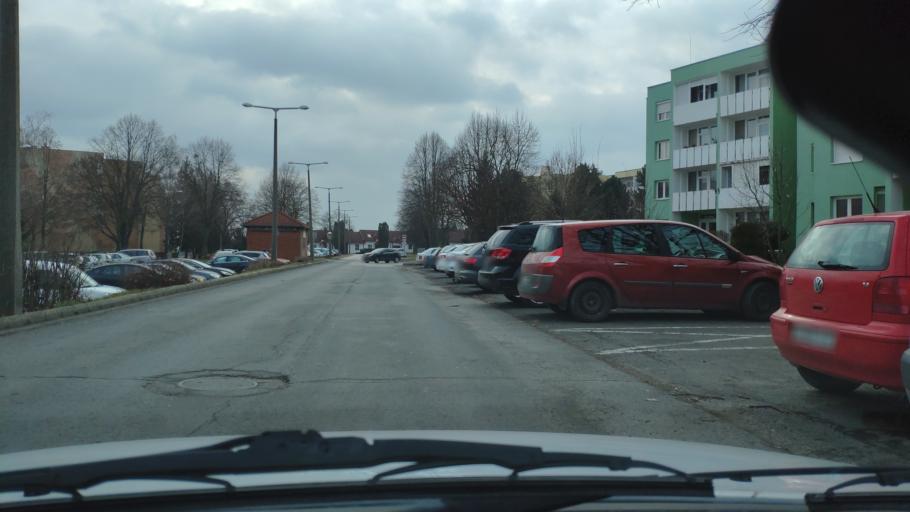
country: HU
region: Zala
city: Nagykanizsa
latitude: 46.4590
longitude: 17.0170
